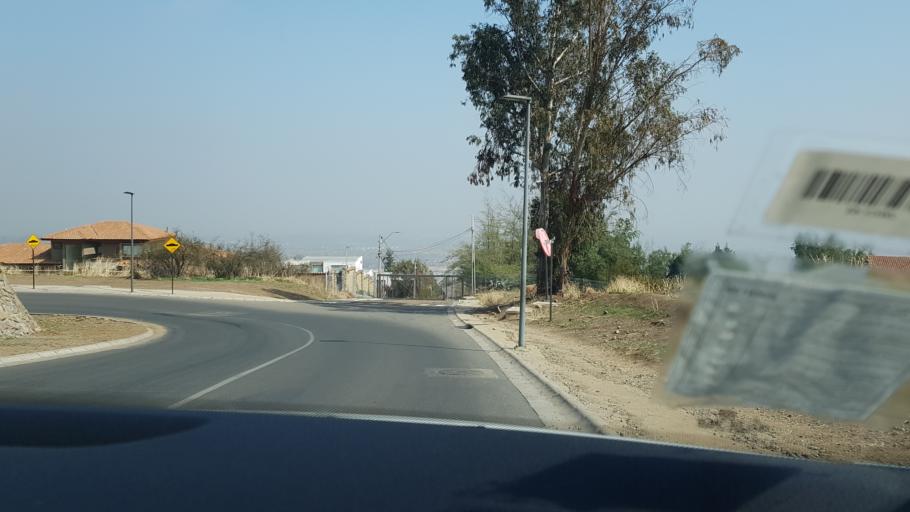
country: CL
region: Santiago Metropolitan
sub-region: Provincia de Santiago
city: Villa Presidente Frei, Nunoa, Santiago, Chile
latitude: -33.4774
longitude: -70.5166
